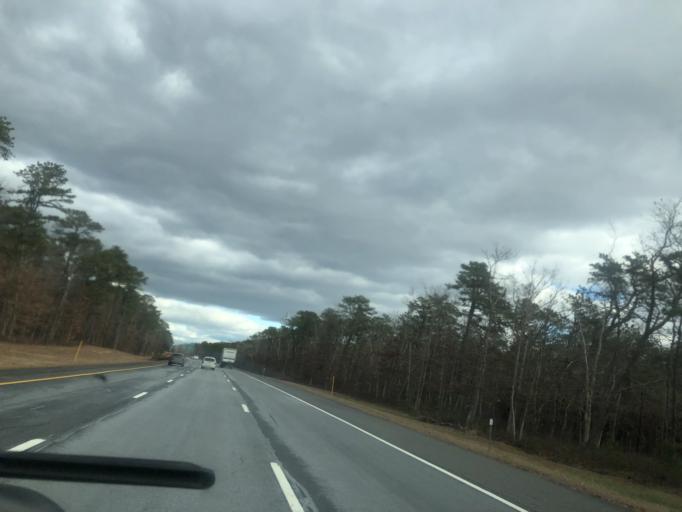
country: US
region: New Jersey
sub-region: Ocean County
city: Tuckerton
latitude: 39.6443
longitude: -74.3597
